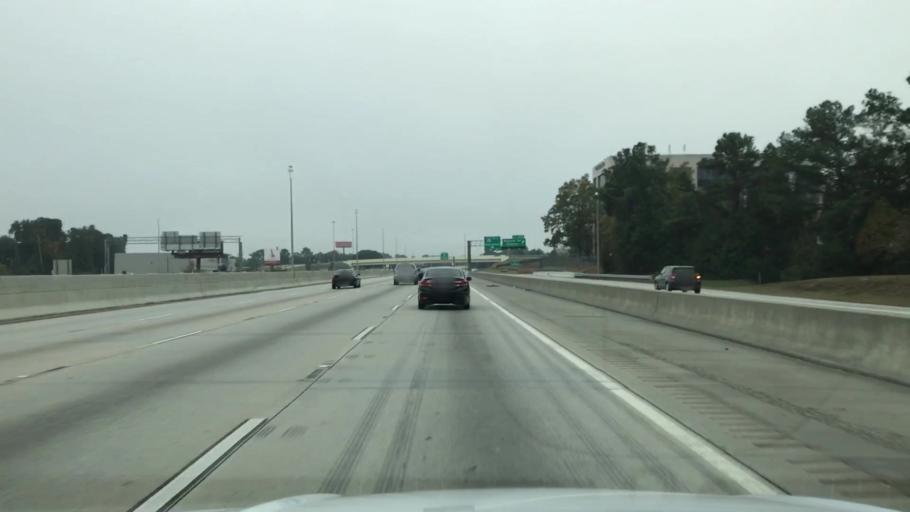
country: US
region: South Carolina
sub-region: Berkeley County
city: Hanahan
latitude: 32.9024
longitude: -80.0233
